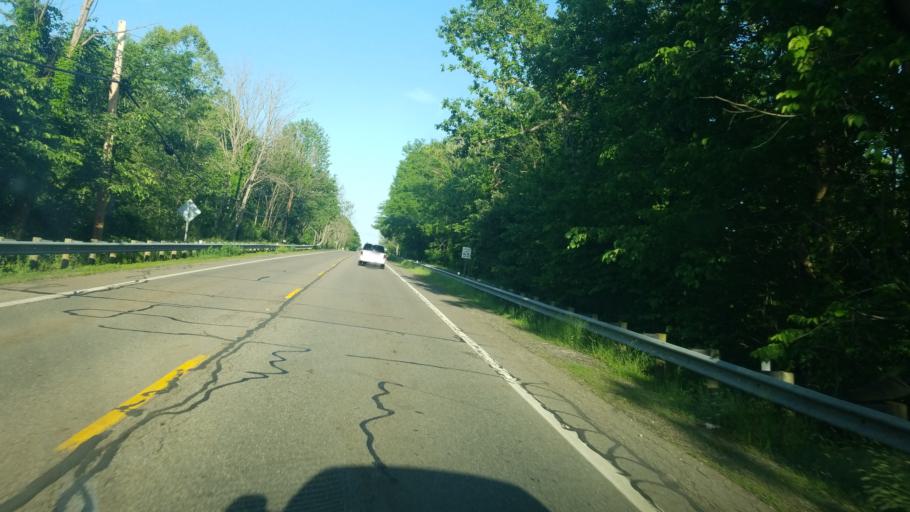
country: US
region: Ohio
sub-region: Portage County
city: Ravenna
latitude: 41.1543
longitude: -81.1956
